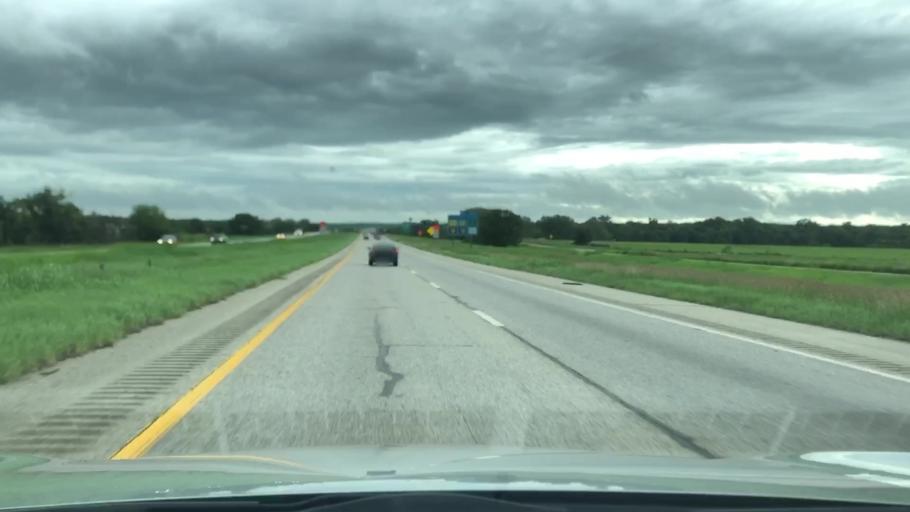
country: US
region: Texas
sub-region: Caldwell County
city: Luling
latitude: 29.6496
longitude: -97.6090
